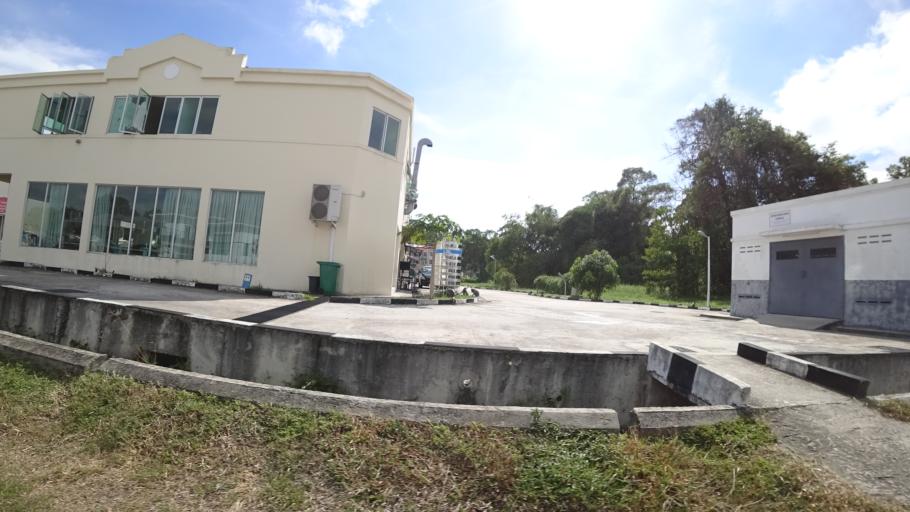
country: BN
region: Brunei and Muara
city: Bandar Seri Begawan
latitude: 4.8899
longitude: 114.8424
